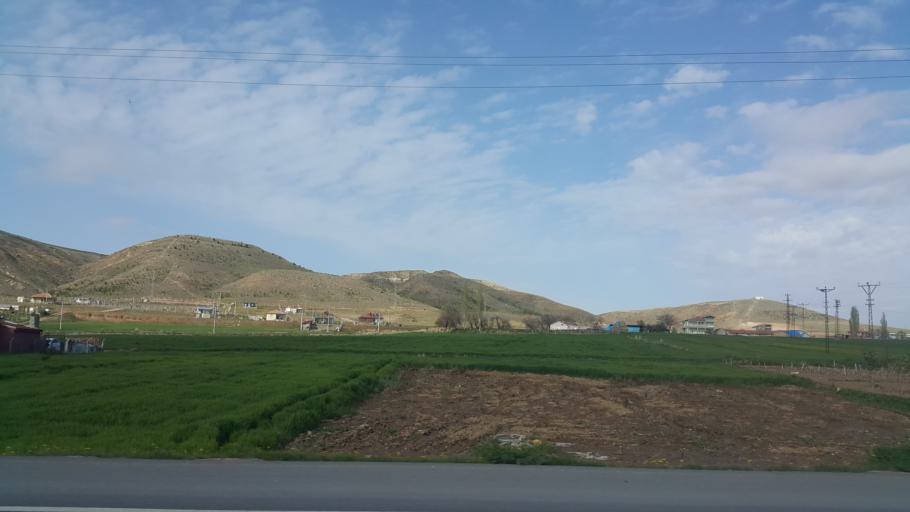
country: TR
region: Aksaray
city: Aksaray
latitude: 38.4396
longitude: 33.9423
